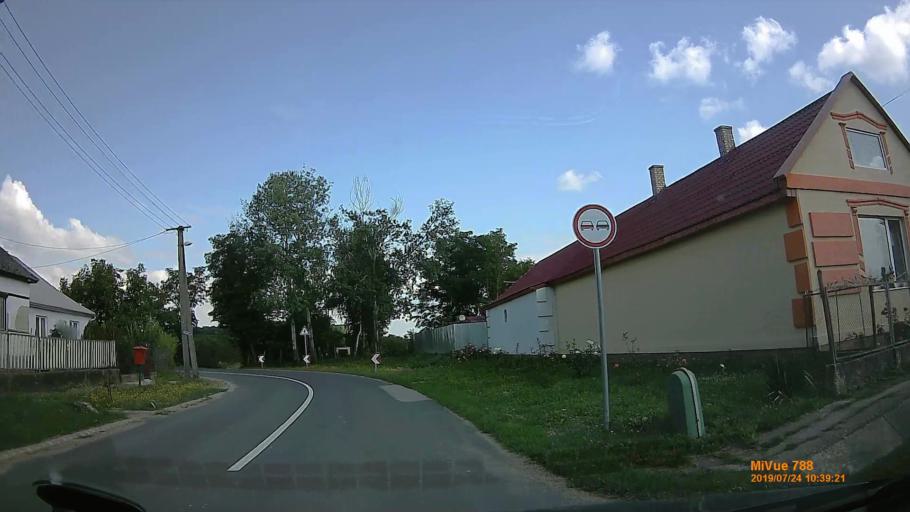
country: HU
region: Szabolcs-Szatmar-Bereg
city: Tarpa
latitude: 48.1651
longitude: 22.5446
